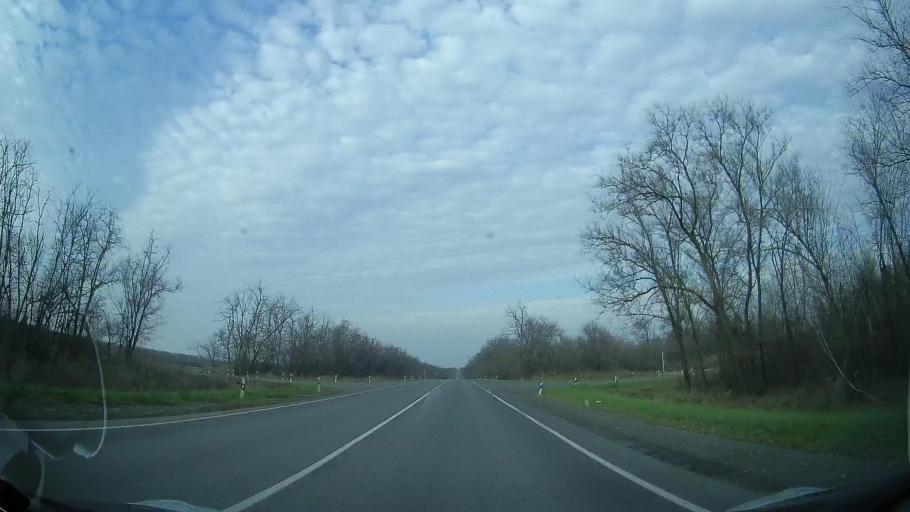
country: RU
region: Rostov
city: Bagayevskaya
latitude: 47.1034
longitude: 40.2767
